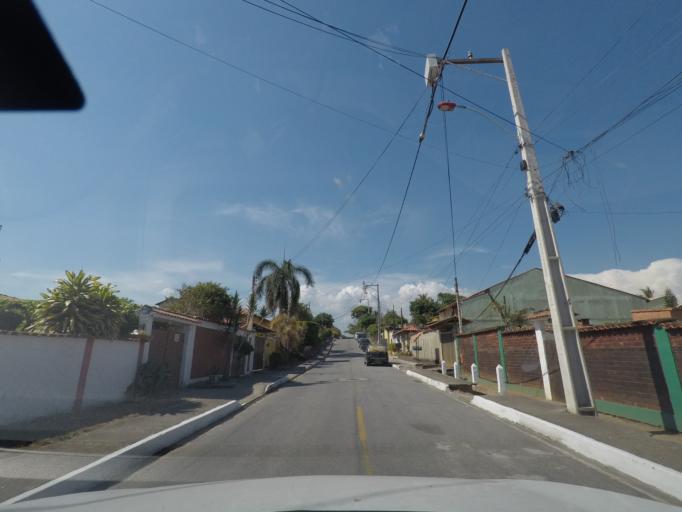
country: BR
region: Rio de Janeiro
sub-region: Niteroi
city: Niteroi
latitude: -22.9673
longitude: -42.9729
